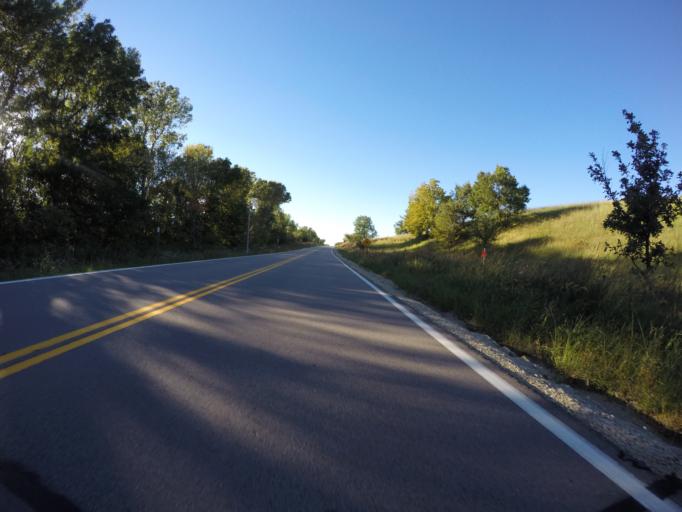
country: US
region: Kansas
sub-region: Riley County
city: Ogden
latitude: 39.2356
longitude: -96.7587
